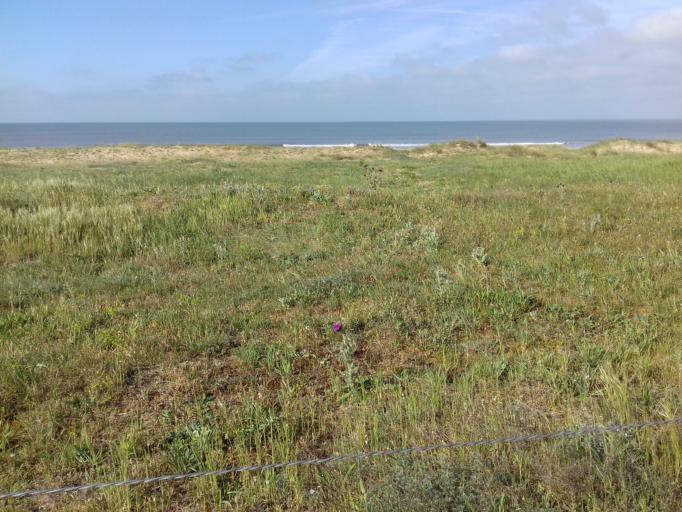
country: FR
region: Pays de la Loire
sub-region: Departement de la Vendee
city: Saint-Jean-de-Monts
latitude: 46.7945
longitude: -2.0969
